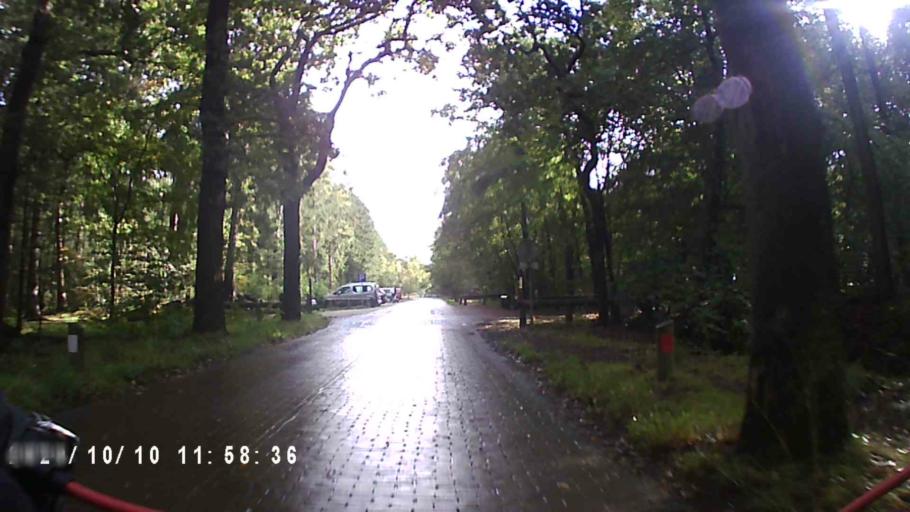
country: NL
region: Friesland
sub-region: Gemeente Smallingerland
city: Drachten
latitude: 53.0587
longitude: 6.0956
